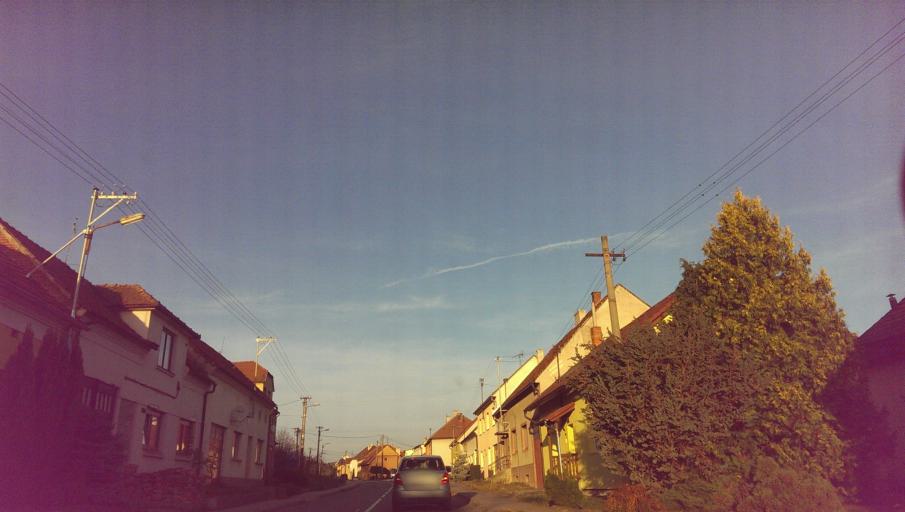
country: CZ
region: Zlin
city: Brezolupy
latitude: 49.1242
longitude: 17.5861
